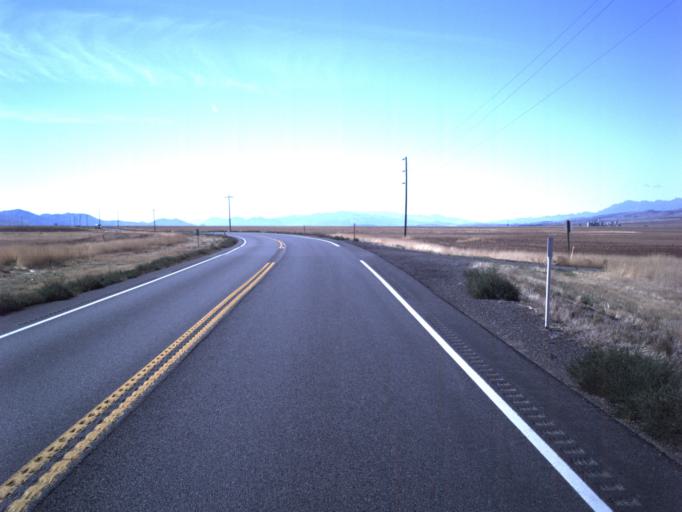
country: US
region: Utah
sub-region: Juab County
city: Nephi
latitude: 39.6463
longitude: -111.8608
